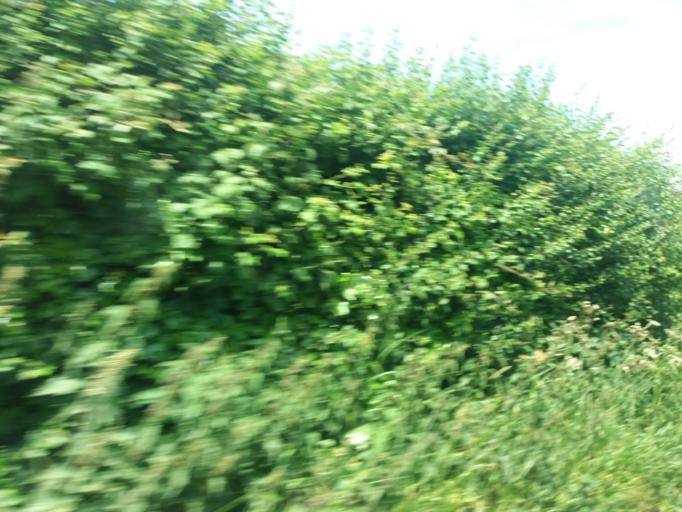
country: IE
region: Leinster
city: Lusk
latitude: 53.5375
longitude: -6.1941
